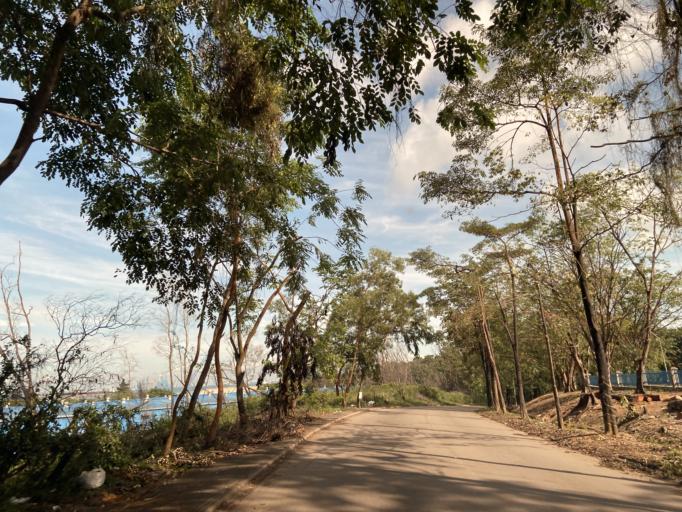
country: SG
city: Singapore
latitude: 1.1752
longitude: 104.0099
